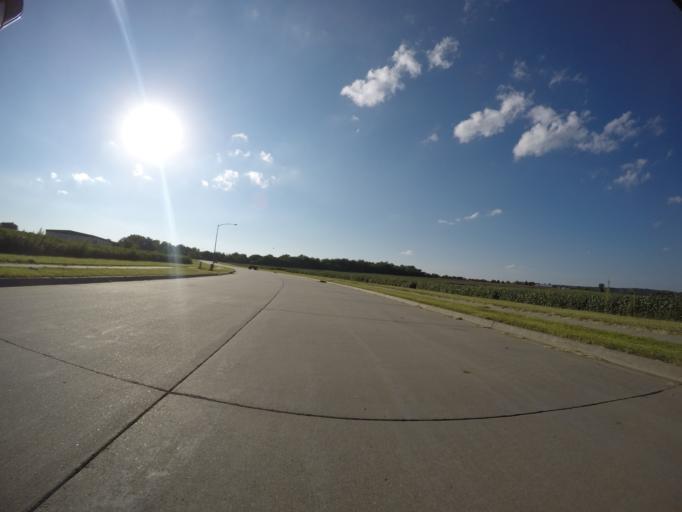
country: US
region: Kansas
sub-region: Riley County
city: Ogden
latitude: 39.1446
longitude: -96.6782
